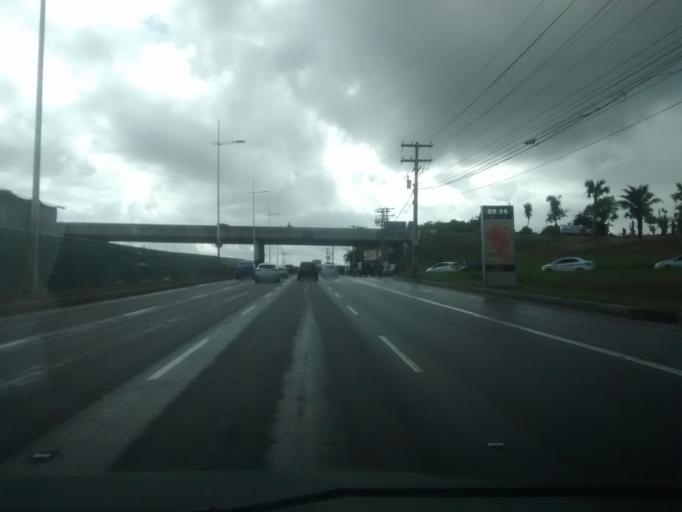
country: BR
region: Bahia
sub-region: Salvador
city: Salvador
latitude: -12.9512
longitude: -38.4251
